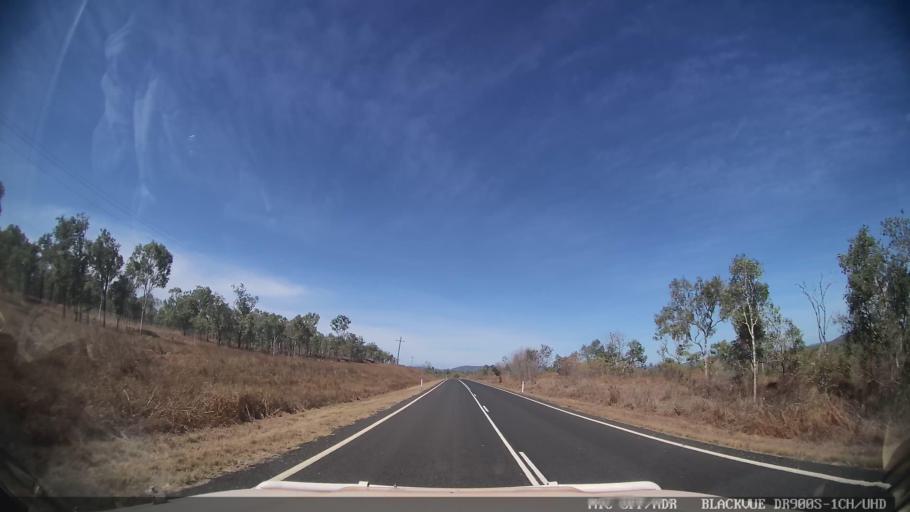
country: AU
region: Queensland
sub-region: Cook
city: Cooktown
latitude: -15.8657
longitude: 144.8139
